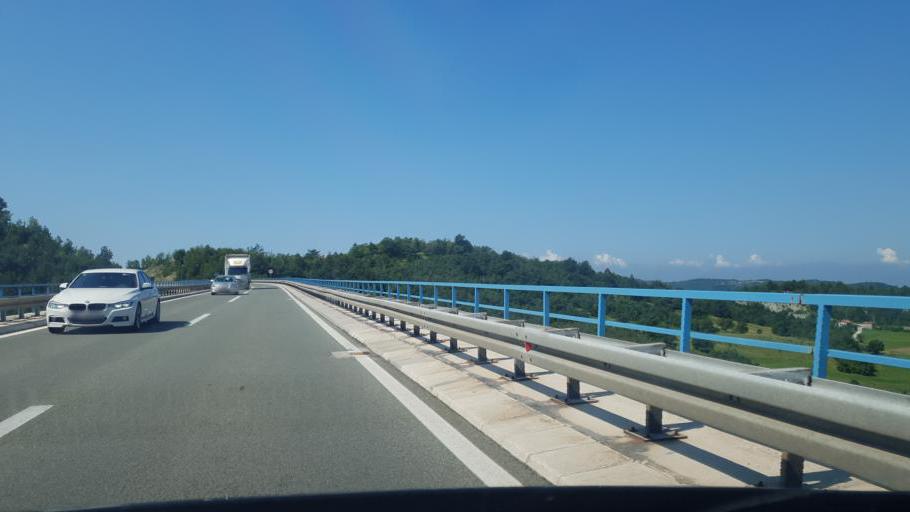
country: HR
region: Istarska
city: Buzet
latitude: 45.3442
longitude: 14.0808
